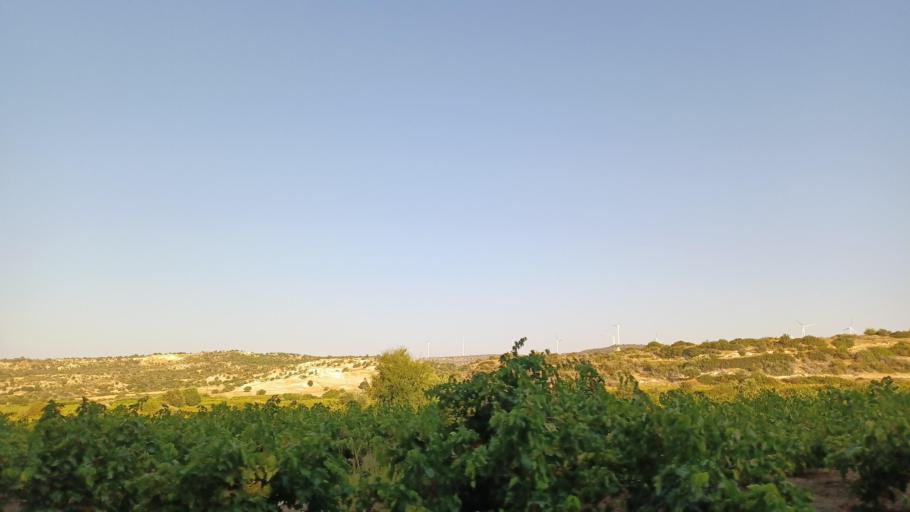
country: CY
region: Limassol
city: Pissouri
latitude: 34.7045
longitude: 32.6769
